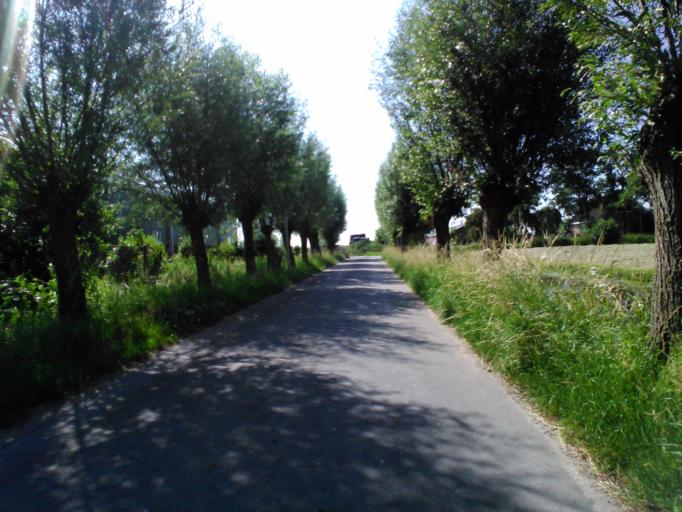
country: NL
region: South Holland
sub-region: Gemeente Alphen aan den Rijn
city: Alphen aan den Rijn
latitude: 52.1049
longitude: 4.6410
